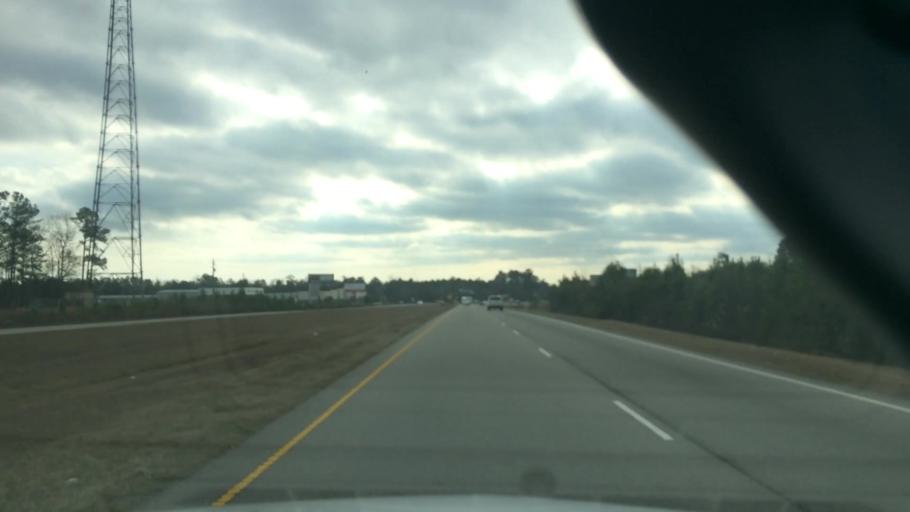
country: US
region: North Carolina
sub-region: Brunswick County
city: Shallotte
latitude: 33.9652
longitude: -78.4149
